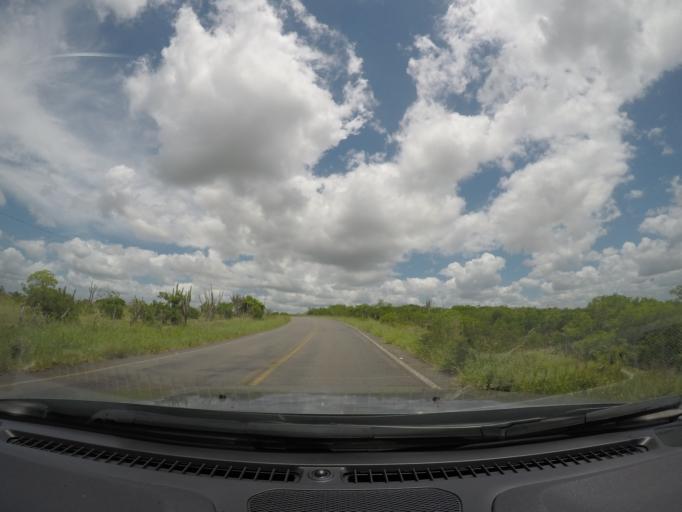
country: BR
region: Bahia
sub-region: Ipira
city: Ipira
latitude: -12.2911
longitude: -39.8765
